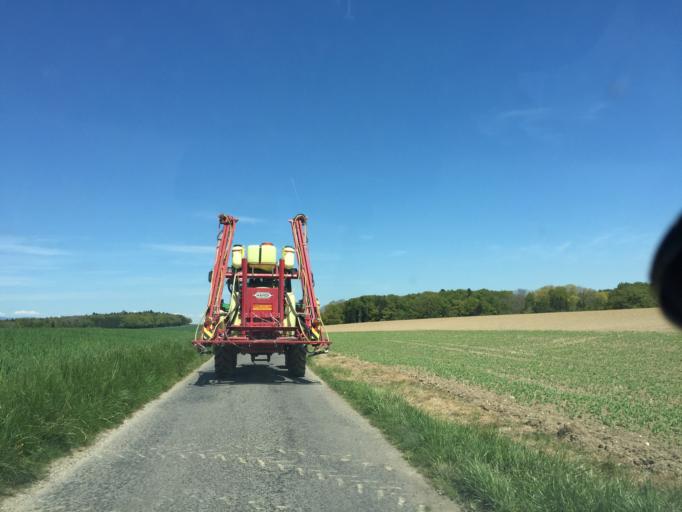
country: CH
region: Vaud
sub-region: Morges District
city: Cuarnens
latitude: 46.6313
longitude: 6.4506
